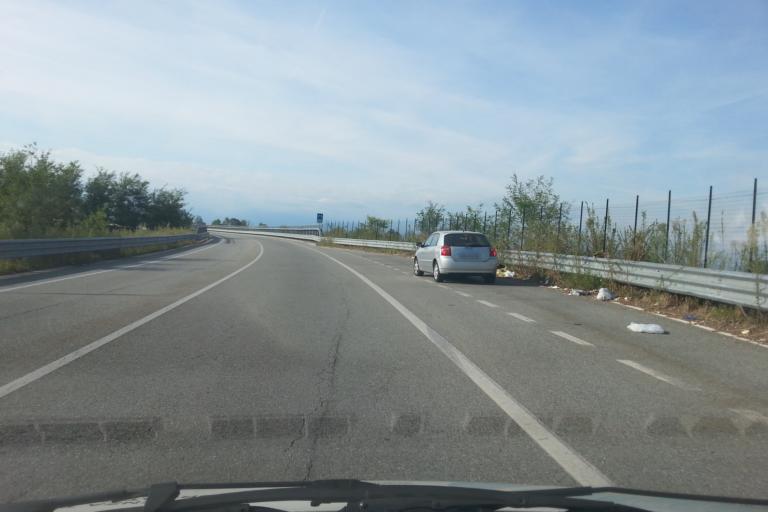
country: IT
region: Piedmont
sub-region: Provincia di Torino
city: San Raffaele Cimena
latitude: 45.1509
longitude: 7.8378
